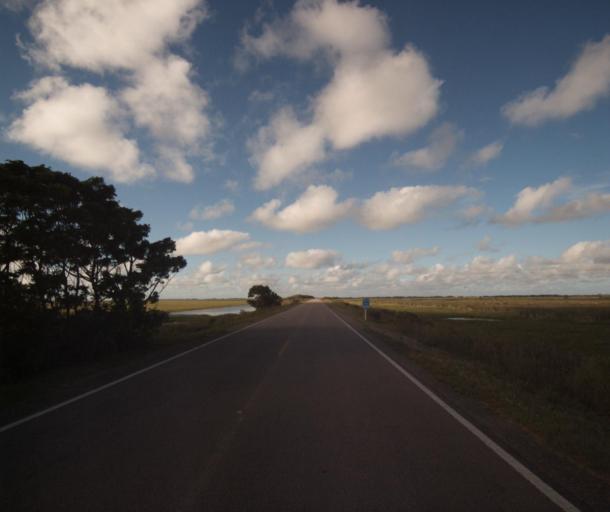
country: BR
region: Rio Grande do Sul
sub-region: Arroio Grande
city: Arroio Grande
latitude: -32.6060
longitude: -52.5714
